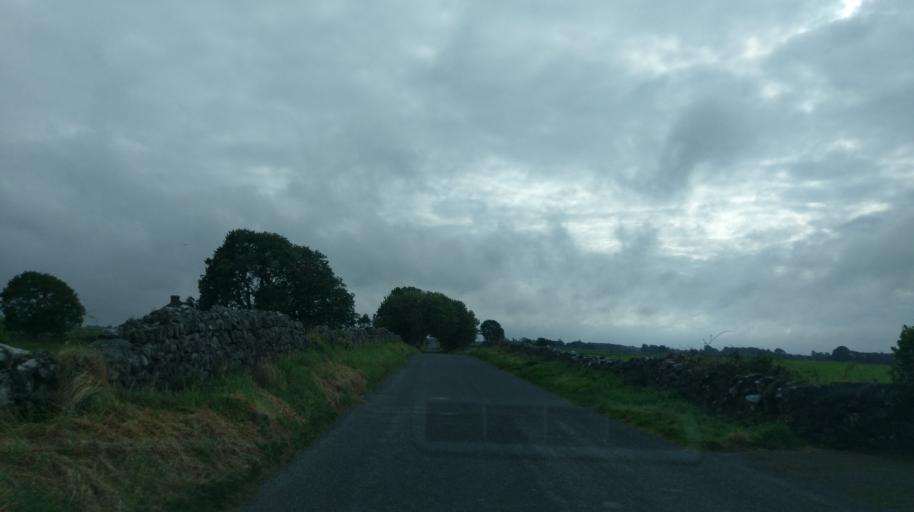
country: IE
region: Connaught
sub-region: County Galway
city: Athenry
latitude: 53.4619
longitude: -8.6262
